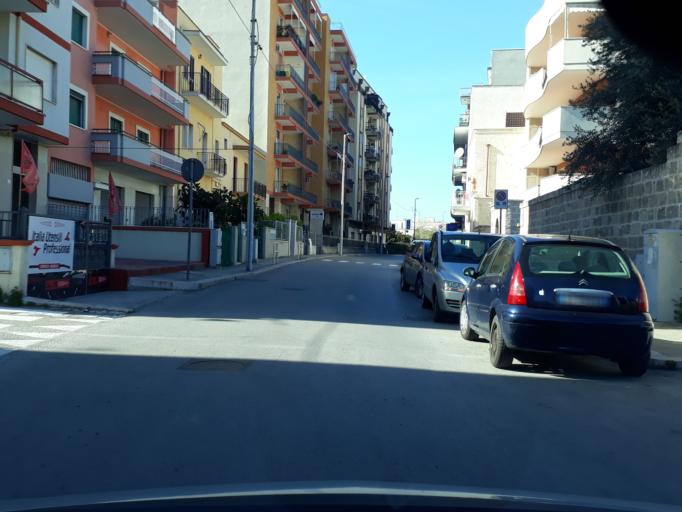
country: IT
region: Apulia
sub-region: Provincia di Bari
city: Monopoli
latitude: 40.9469
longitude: 17.2997
